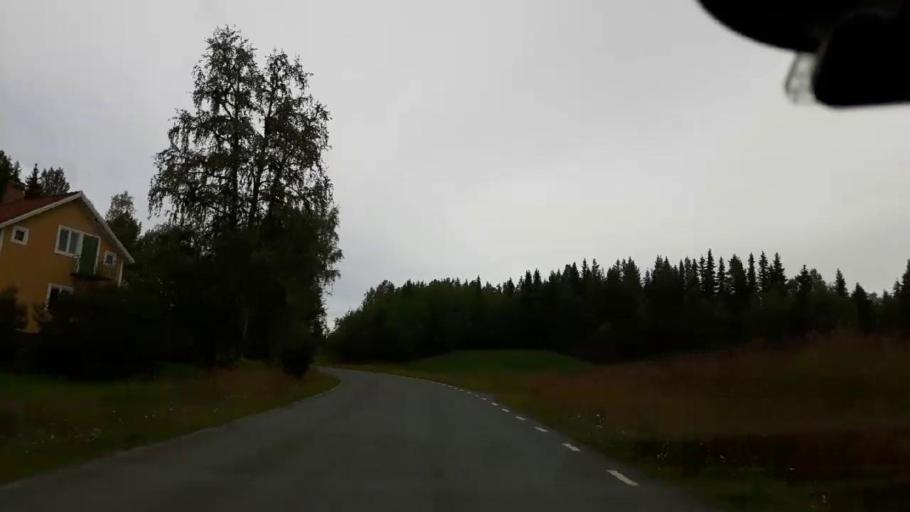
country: SE
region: Jaemtland
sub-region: Krokoms Kommun
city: Valla
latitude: 63.6522
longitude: 13.8296
